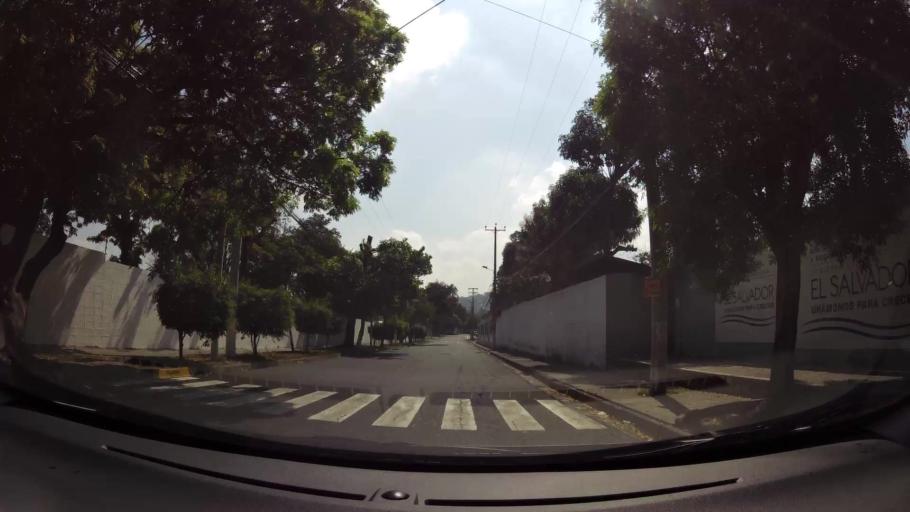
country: SV
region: La Libertad
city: Antiguo Cuscatlan
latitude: 13.6883
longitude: -89.2309
